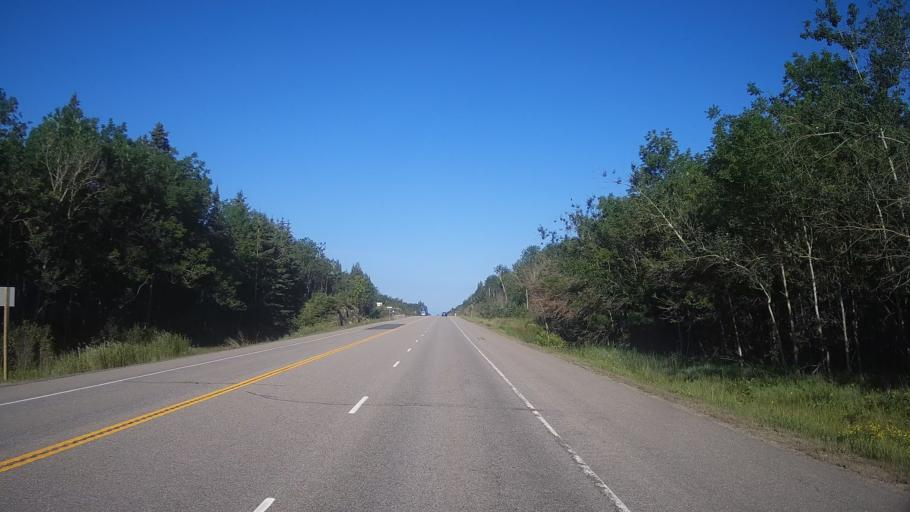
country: US
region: Minnesota
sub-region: Roseau County
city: Warroad
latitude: 49.7184
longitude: -94.7343
